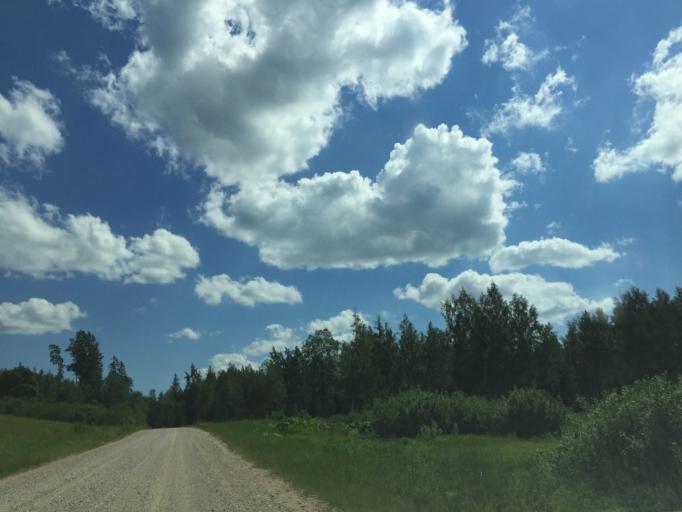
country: LV
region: Priekuli
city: Priekuli
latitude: 57.2509
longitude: 25.4325
